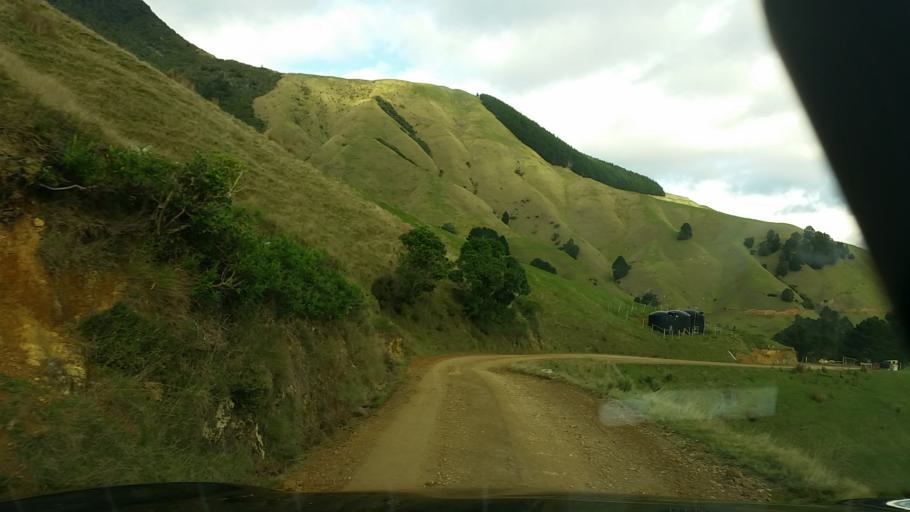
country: NZ
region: Marlborough
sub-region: Marlborough District
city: Picton
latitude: -40.9902
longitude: 173.8318
